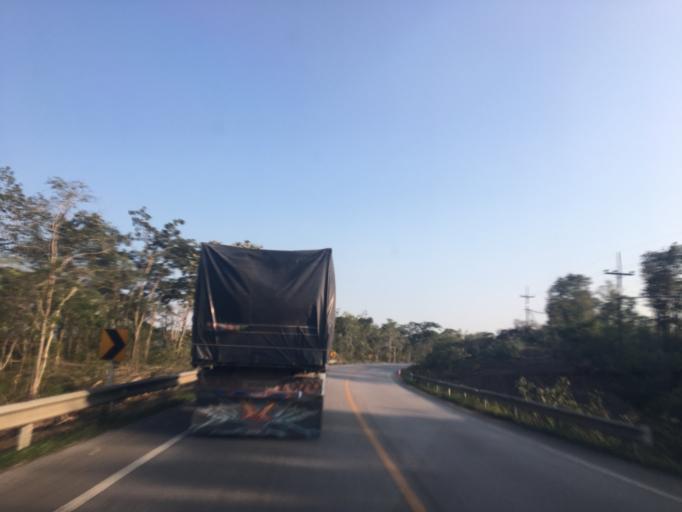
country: TH
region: Lampang
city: Ngao
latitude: 18.6631
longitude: 100.0167
